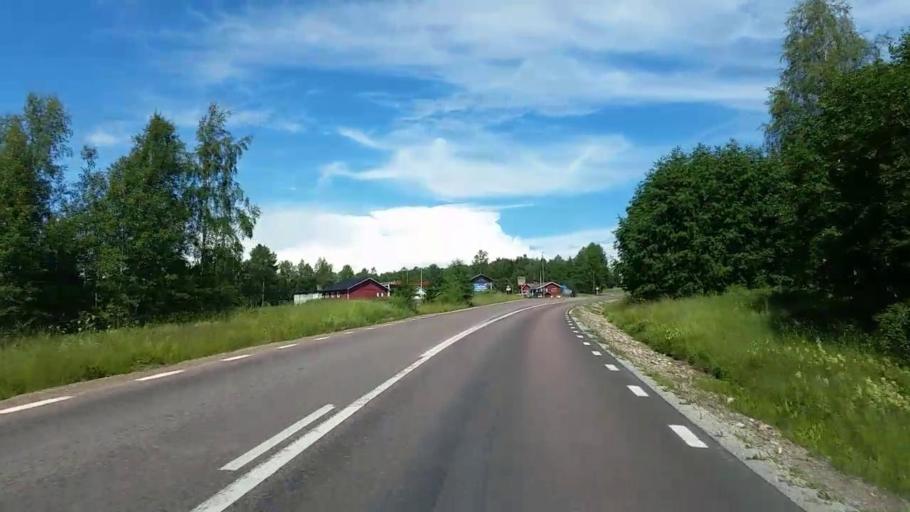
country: SE
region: Dalarna
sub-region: Rattviks Kommun
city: Raettvik
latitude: 61.0027
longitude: 15.2185
